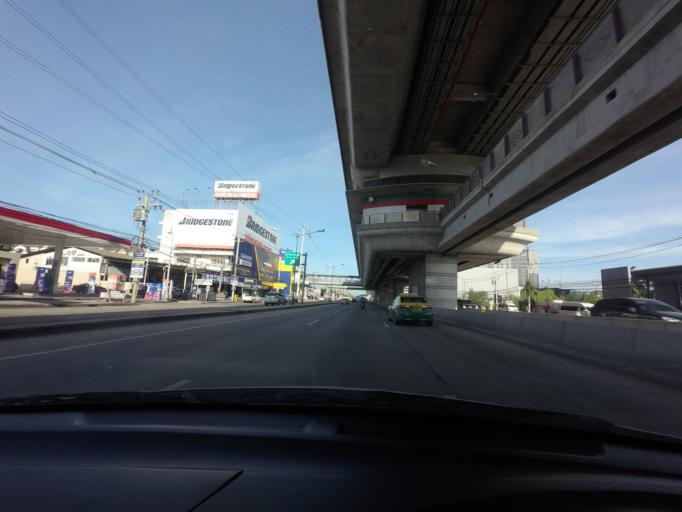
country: TH
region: Nonthaburi
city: Bang Bua Thong
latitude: 13.8746
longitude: 100.4192
